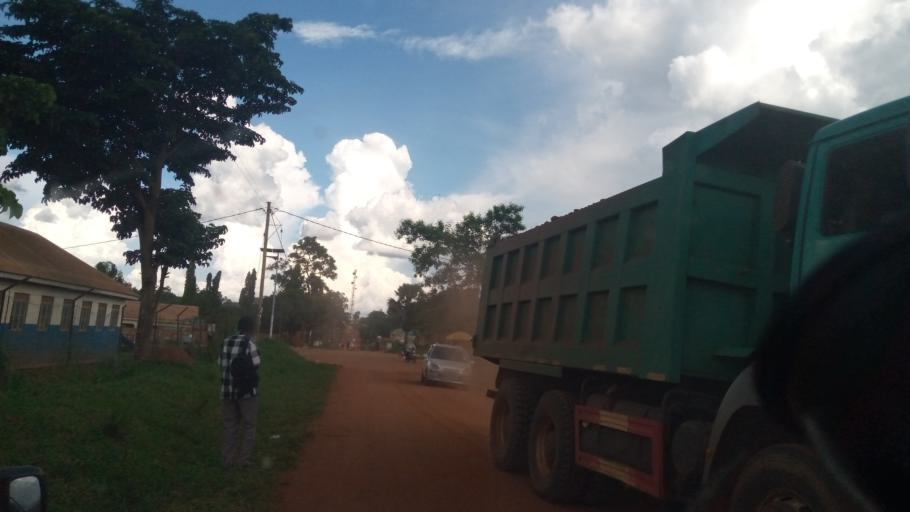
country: UG
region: Northern Region
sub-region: Lira District
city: Lira
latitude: 2.2392
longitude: 32.8988
